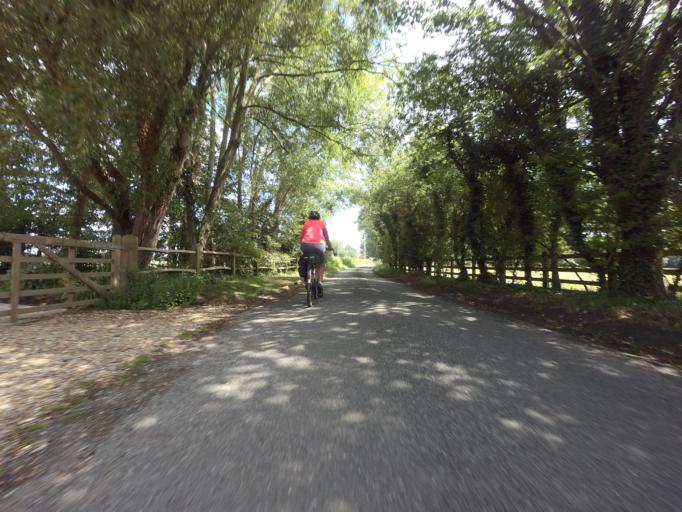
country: GB
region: England
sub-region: Kent
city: Stone
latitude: 50.9955
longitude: 0.8110
